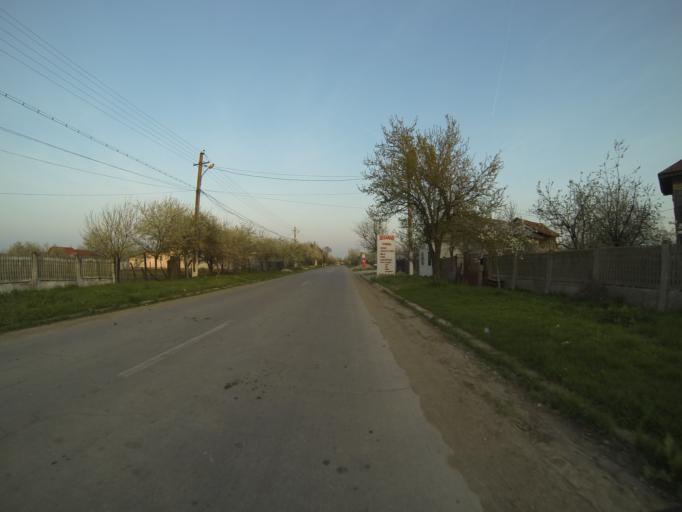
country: RO
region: Dolj
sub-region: Comuna Dranicu
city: Dranic
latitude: 44.0572
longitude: 23.8345
